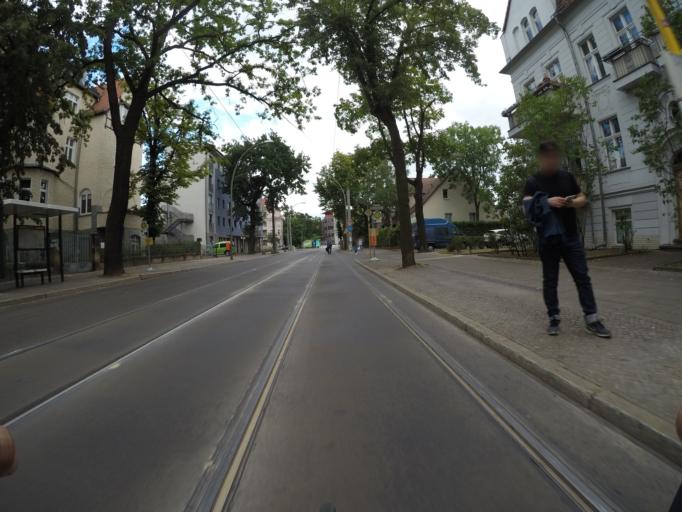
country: DE
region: Berlin
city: Karlshorst
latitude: 52.4790
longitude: 13.5233
